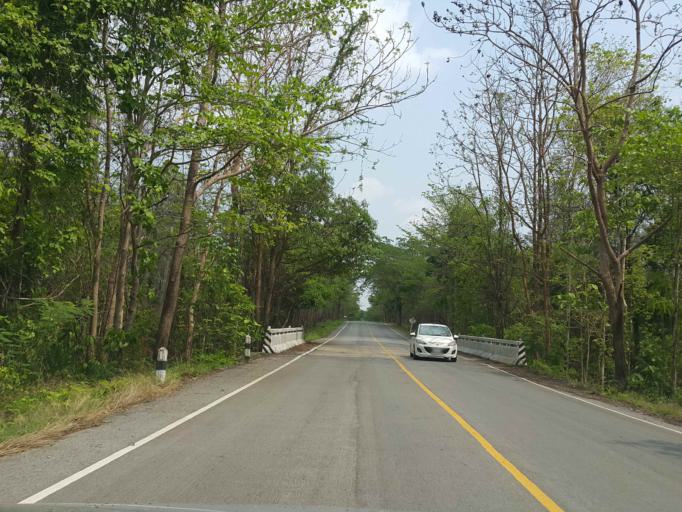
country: TH
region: Sukhothai
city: Thung Saliam
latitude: 17.3954
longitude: 99.3925
